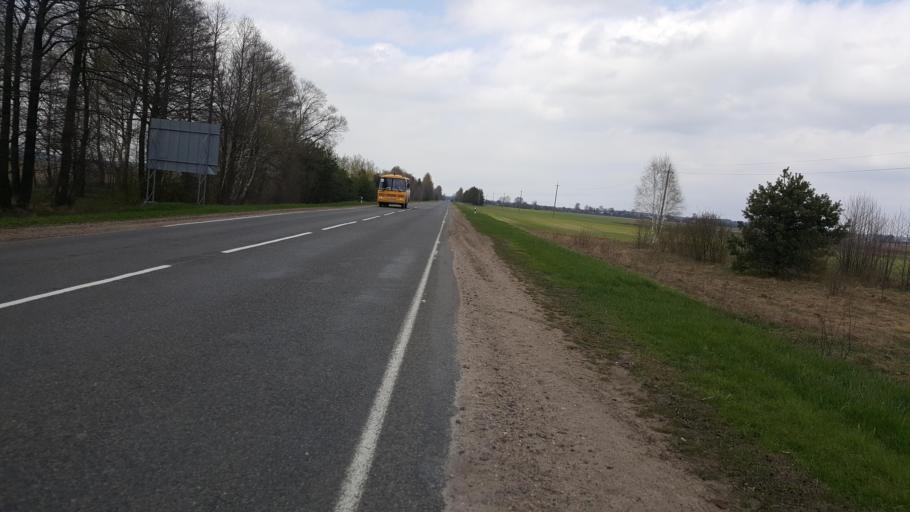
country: BY
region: Brest
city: Kamyanyets
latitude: 52.3461
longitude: 23.9033
